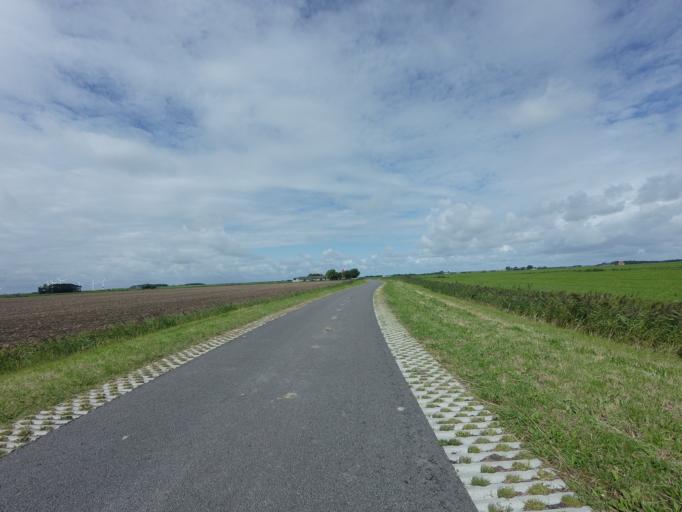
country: NL
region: Friesland
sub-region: Sudwest Fryslan
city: Makkum
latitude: 53.0972
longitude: 5.4176
